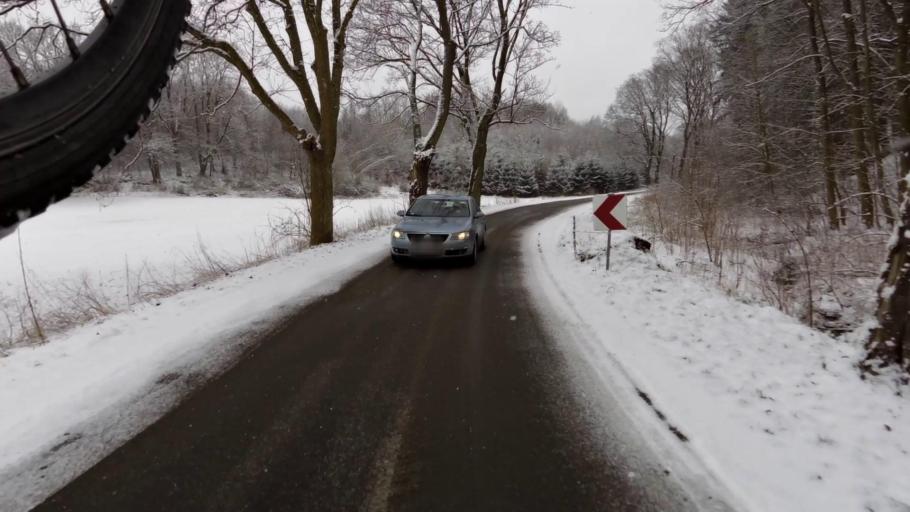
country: PL
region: West Pomeranian Voivodeship
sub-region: Powiat swidwinski
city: Rabino
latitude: 53.8830
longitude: 15.9340
